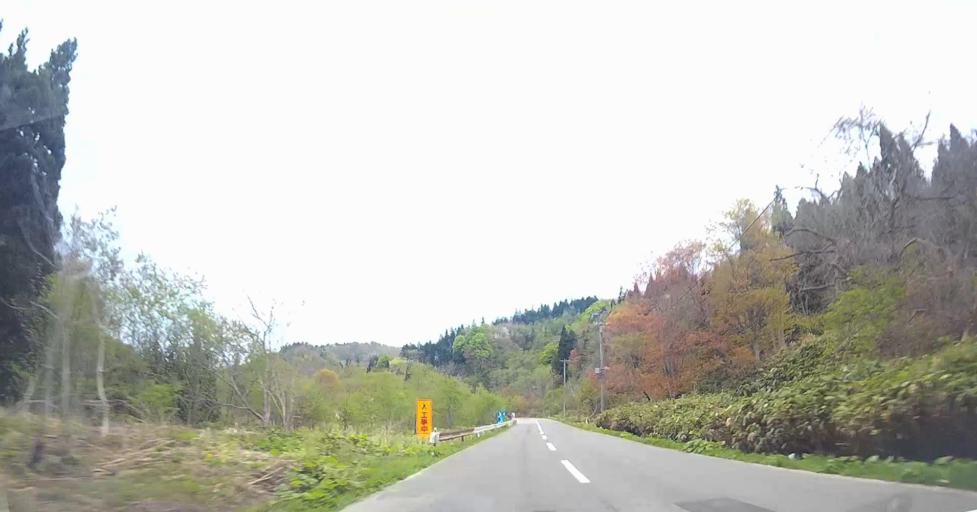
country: JP
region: Aomori
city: Goshogawara
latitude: 41.1202
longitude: 140.5235
